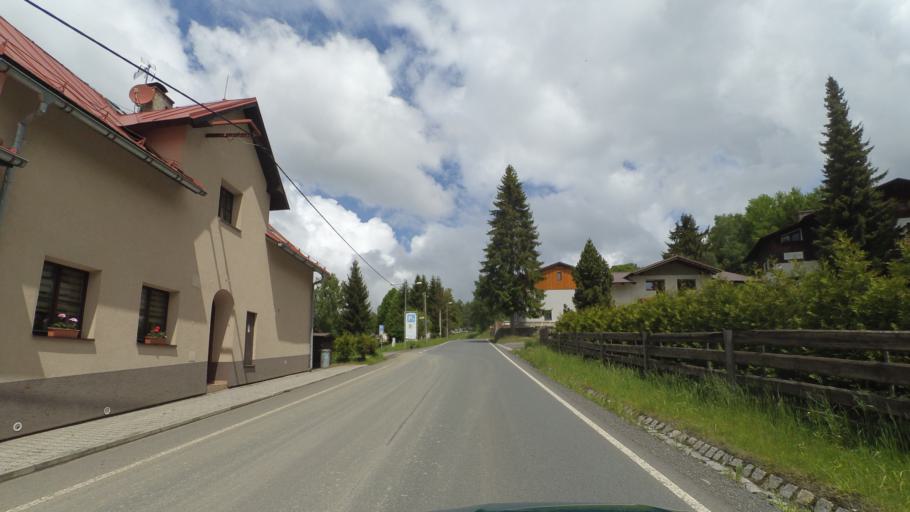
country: CZ
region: Plzensky
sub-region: Okres Klatovy
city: Zelezna Ruda
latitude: 49.1574
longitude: 13.2264
